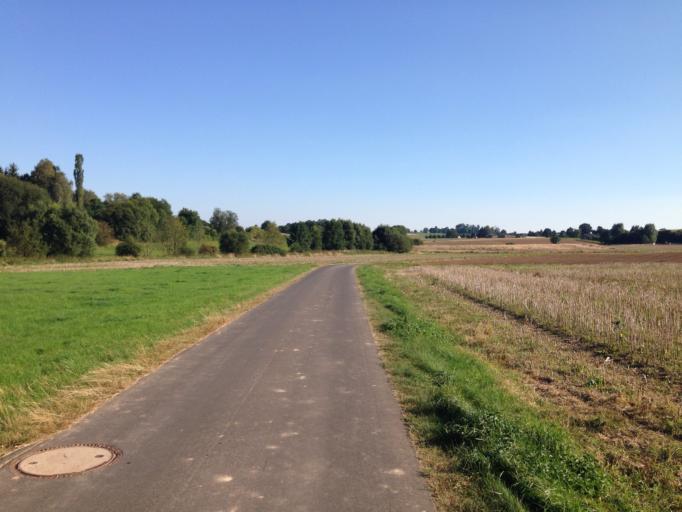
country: DE
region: Hesse
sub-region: Regierungsbezirk Giessen
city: Grunberg
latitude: 50.6270
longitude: 8.9400
